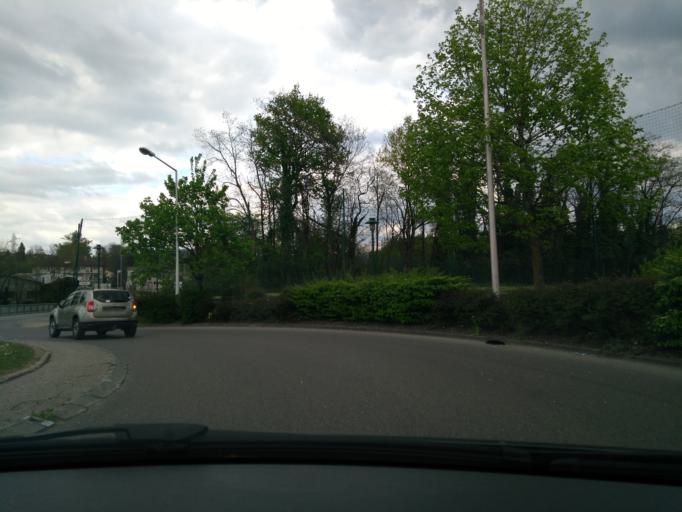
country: FR
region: Rhone-Alpes
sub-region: Departement de la Haute-Savoie
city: Rumilly
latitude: 45.8712
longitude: 5.9398
